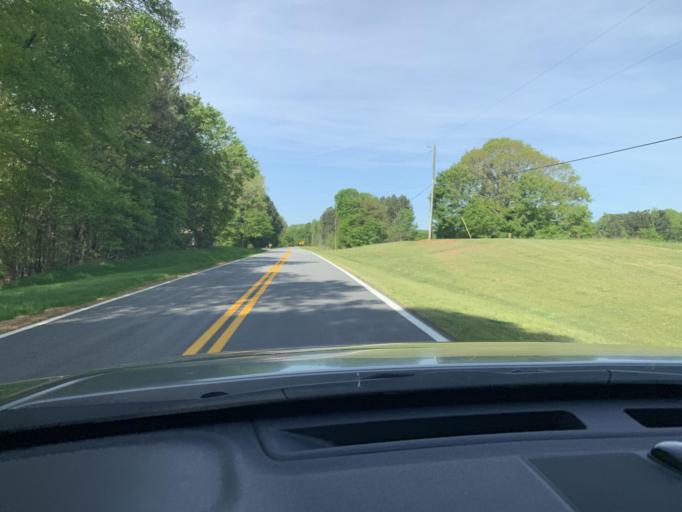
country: US
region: Georgia
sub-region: Oconee County
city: Watkinsville
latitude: 33.8180
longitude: -83.3705
